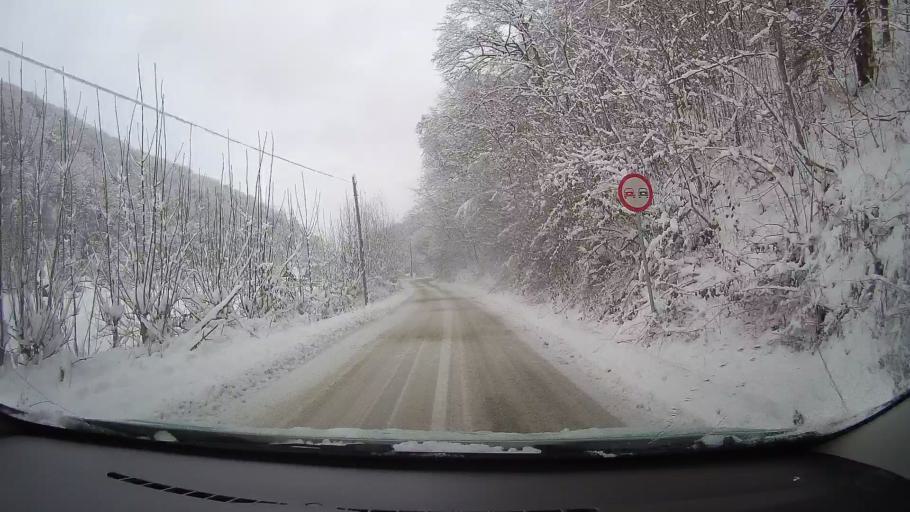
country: RO
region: Alba
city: Pianu de Sus
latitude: 45.8639
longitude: 23.4982
